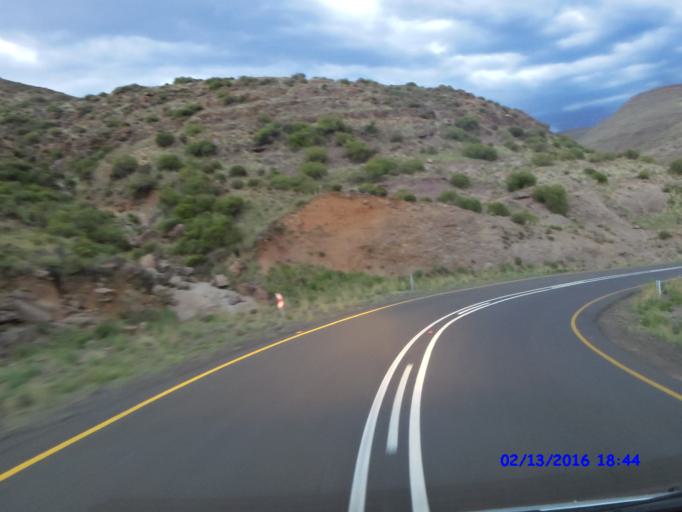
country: LS
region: Qacha's Nek
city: Qacha's Nek
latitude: -30.0517
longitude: 28.3041
